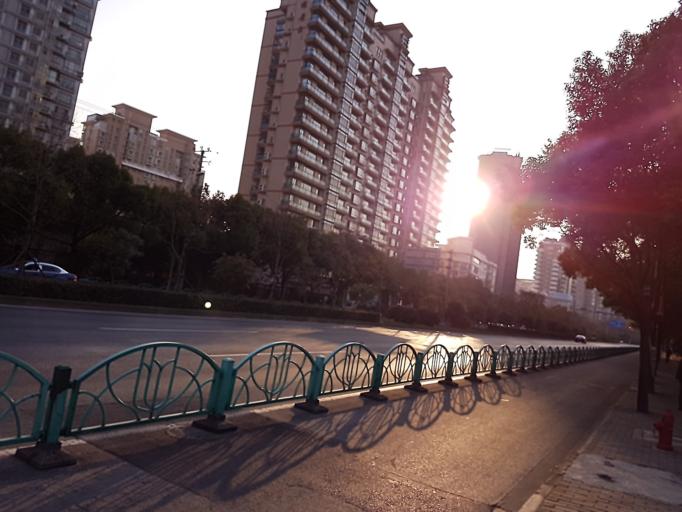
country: CN
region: Shanghai Shi
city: Huamu
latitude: 31.2139
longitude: 121.5494
